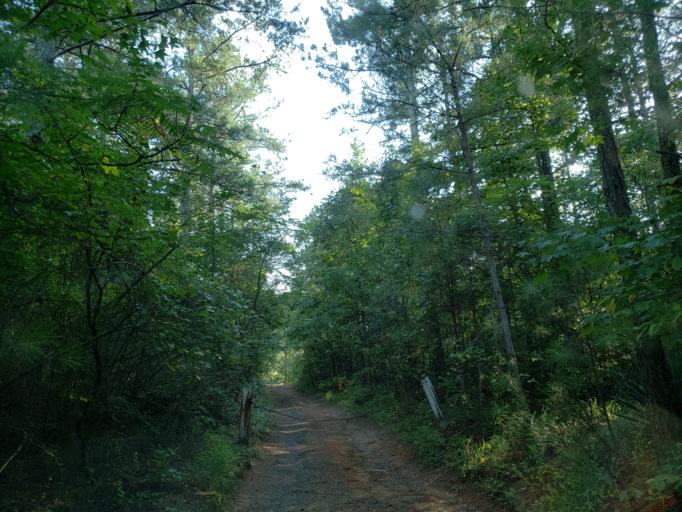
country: US
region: Georgia
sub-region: Cobb County
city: Acworth
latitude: 34.1827
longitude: -84.6460
